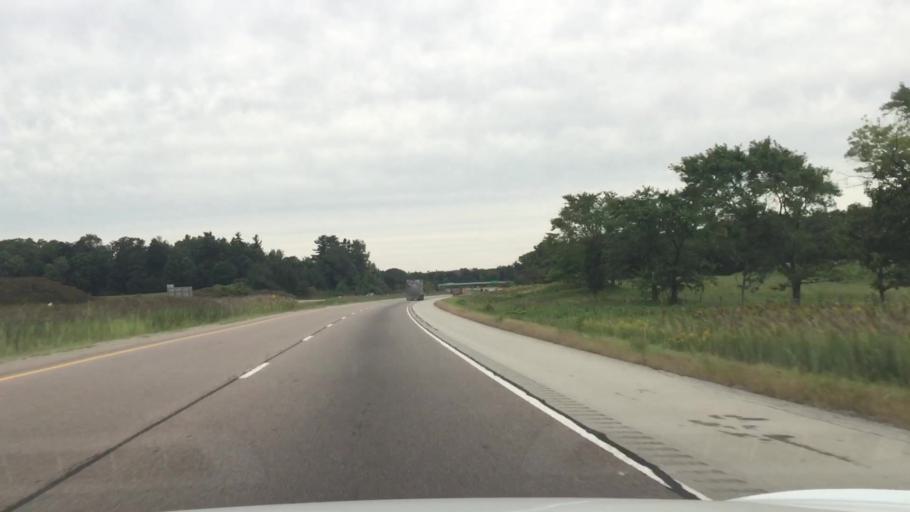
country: CA
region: Ontario
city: Delaware
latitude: 42.9125
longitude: -81.4589
